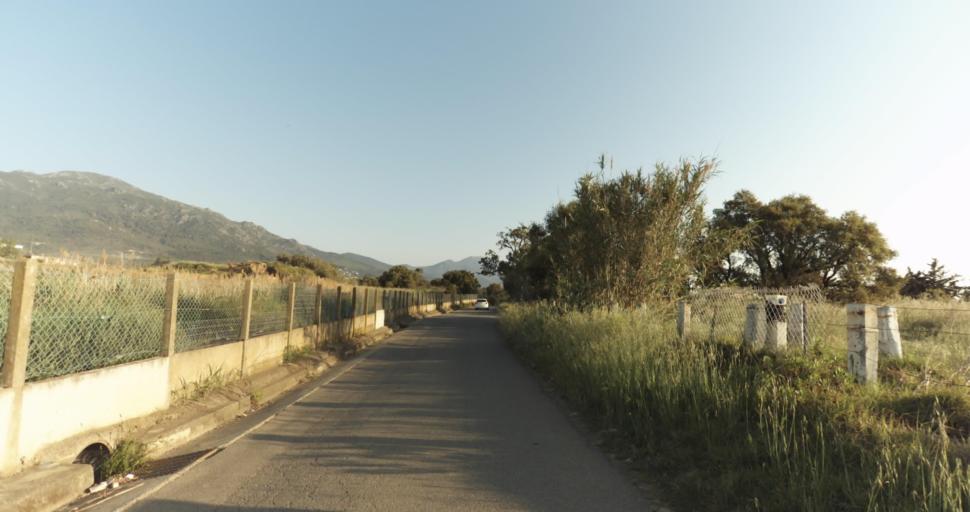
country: FR
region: Corsica
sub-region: Departement de la Haute-Corse
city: Biguglia
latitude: 42.6041
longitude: 9.4447
